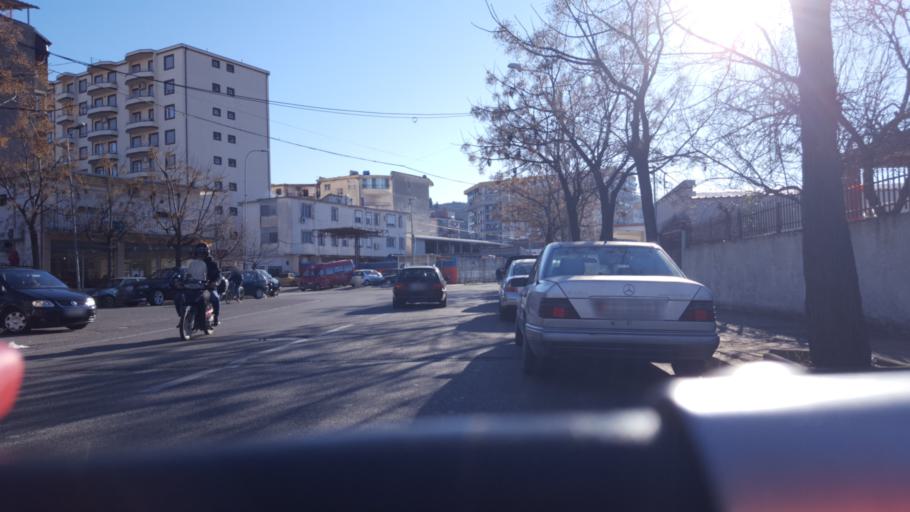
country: AL
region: Shkoder
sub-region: Rrethi i Shkodres
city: Shkoder
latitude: 42.0586
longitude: 19.5007
